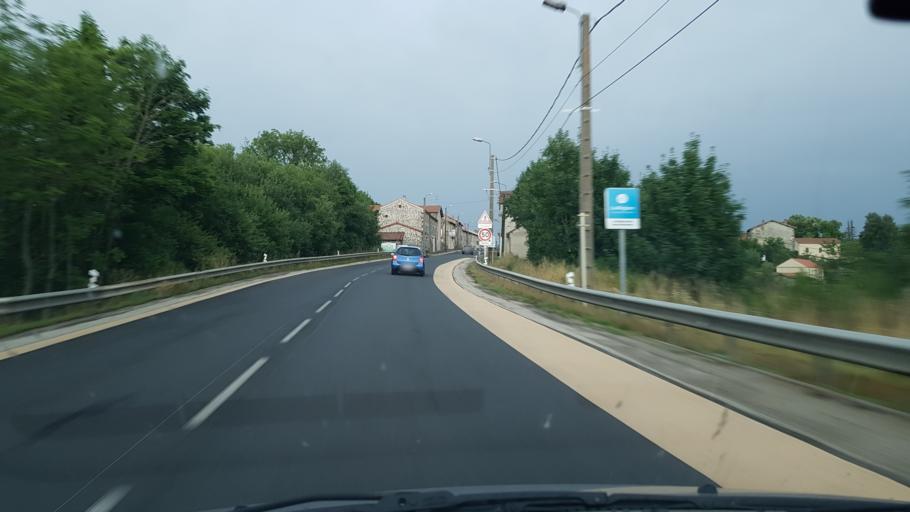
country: FR
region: Auvergne
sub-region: Departement de la Haute-Loire
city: Allegre
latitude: 45.1454
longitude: 3.6658
